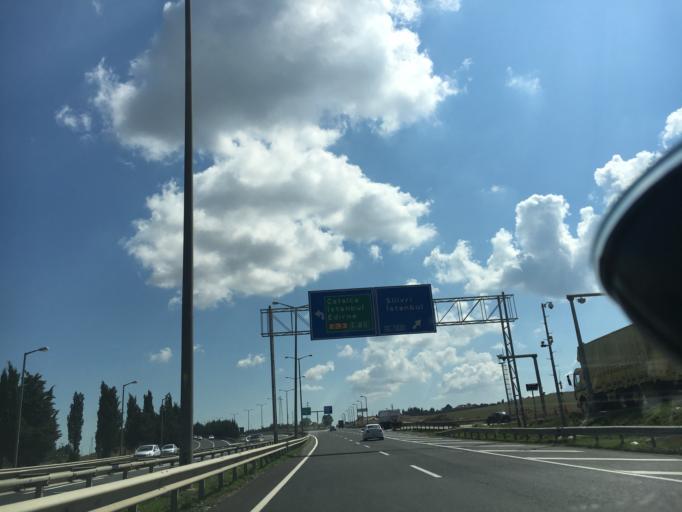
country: TR
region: Istanbul
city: Canta
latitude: 41.0711
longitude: 28.1147
